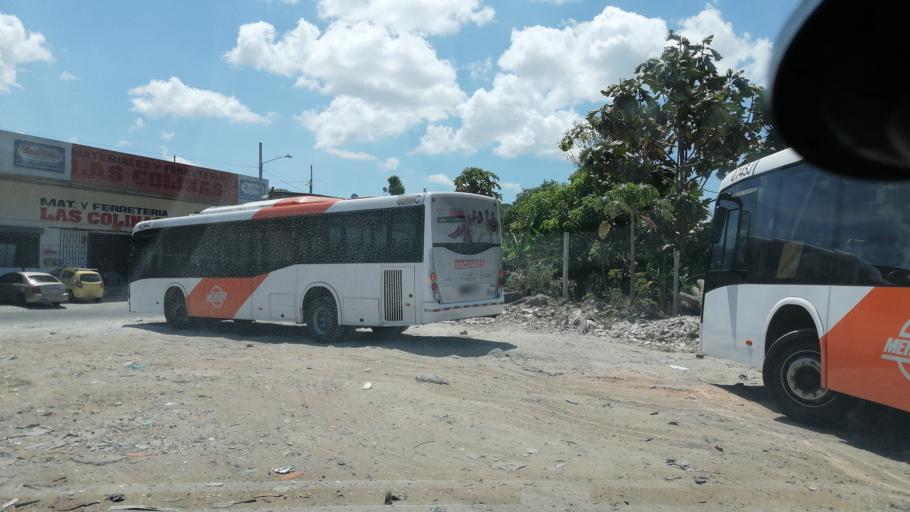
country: PA
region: Panama
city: San Miguelito
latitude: 9.0557
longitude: -79.4899
